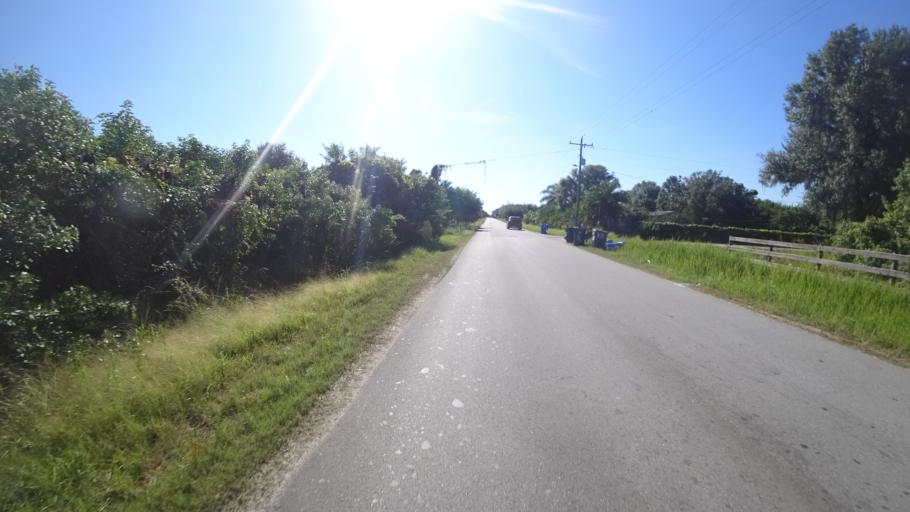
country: US
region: Florida
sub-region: Hillsborough County
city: Sun City Center
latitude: 27.6600
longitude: -82.3570
